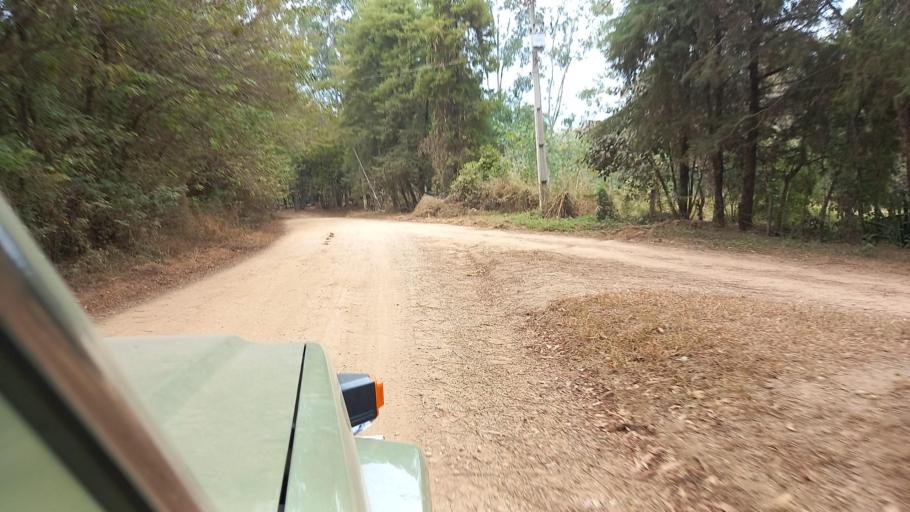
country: BR
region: Sao Paulo
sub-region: Moji-Guacu
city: Mogi-Gaucu
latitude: -22.3082
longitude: -46.8351
